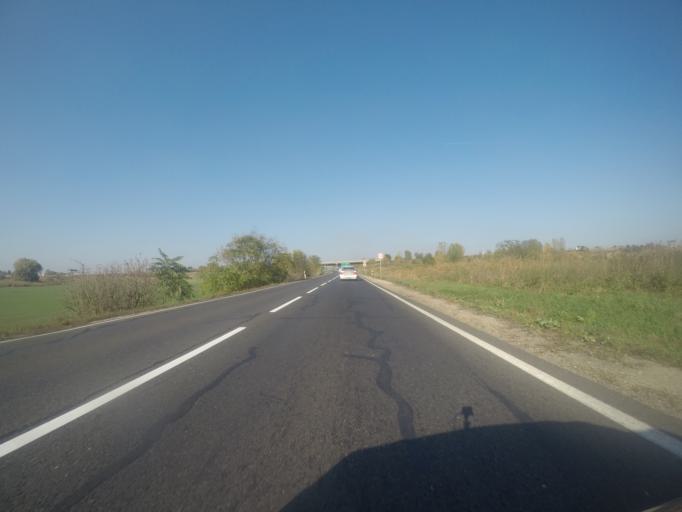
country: HU
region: Fejer
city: Baracs
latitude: 46.9079
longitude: 18.9256
